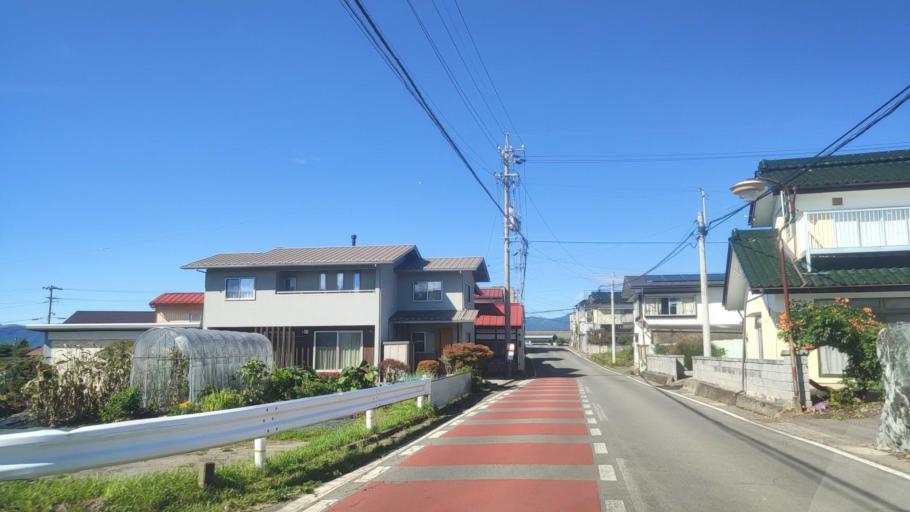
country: JP
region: Nagano
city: Chino
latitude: 35.9773
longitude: 138.2190
